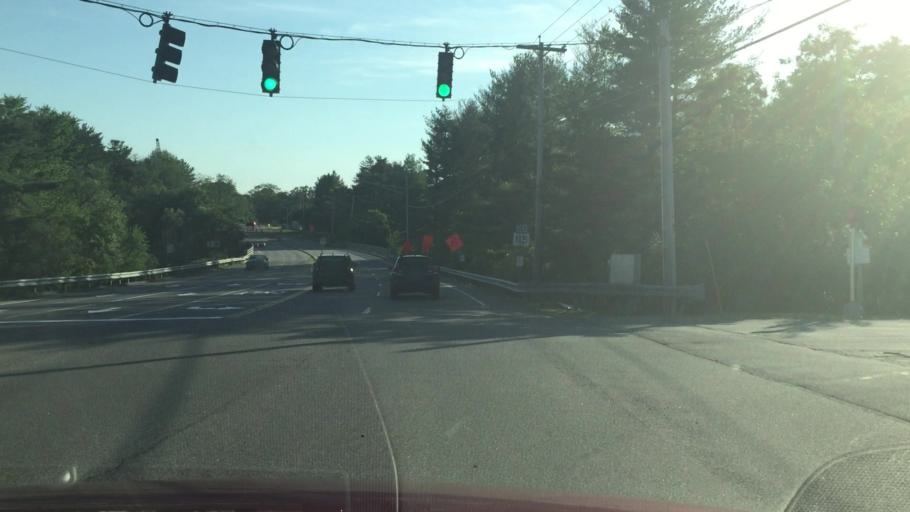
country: US
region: Maine
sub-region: Cumberland County
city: Yarmouth
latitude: 43.8033
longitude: -70.1827
